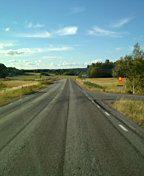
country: SE
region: Uppsala
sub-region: Habo Kommun
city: Balsta
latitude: 59.6542
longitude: 17.5579
